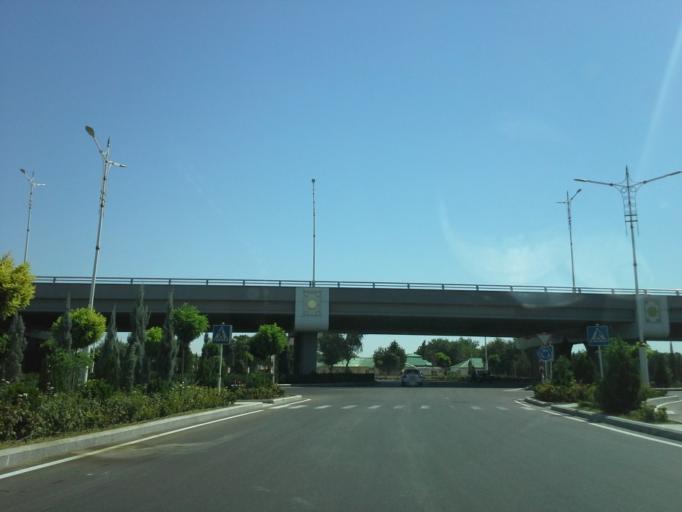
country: TM
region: Ahal
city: Ashgabat
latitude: 37.9619
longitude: 58.3620
